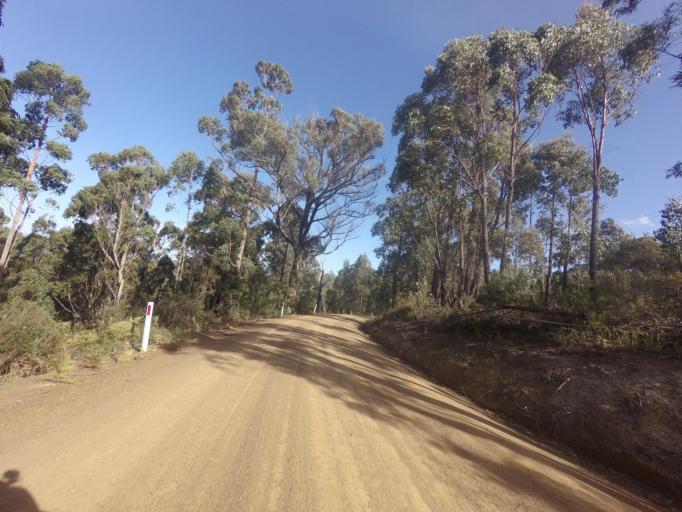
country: AU
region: Tasmania
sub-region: Kingborough
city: Kettering
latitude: -43.0947
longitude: 147.2633
